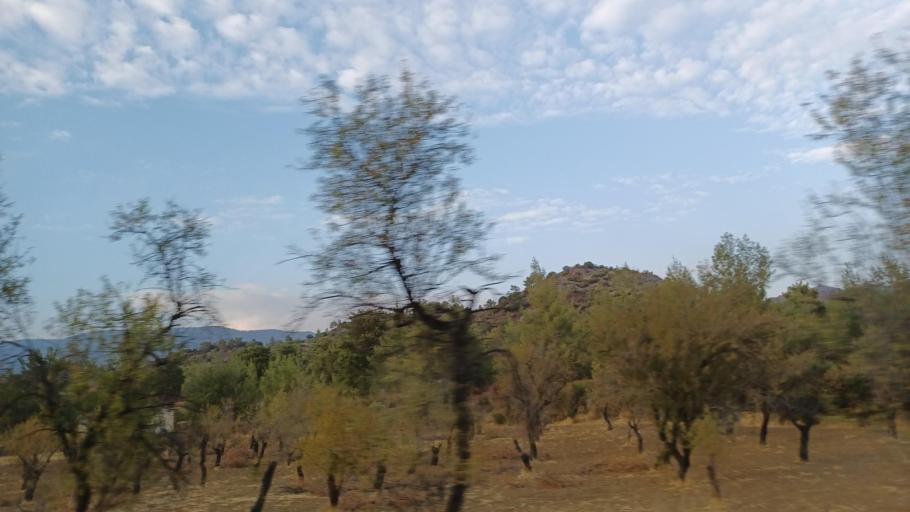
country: CY
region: Limassol
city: Pelendri
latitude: 34.8587
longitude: 32.9269
